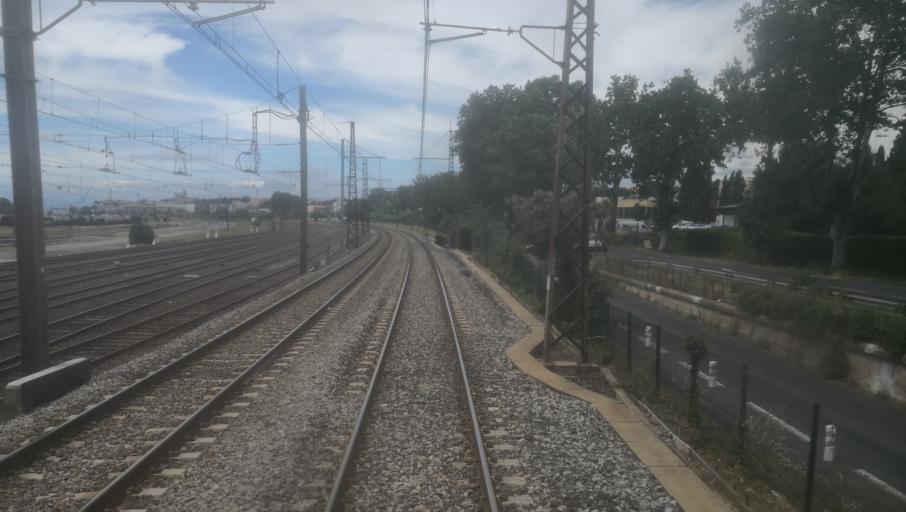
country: FR
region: Languedoc-Roussillon
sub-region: Departement de l'Herault
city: Beziers
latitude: 43.3286
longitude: 3.2425
